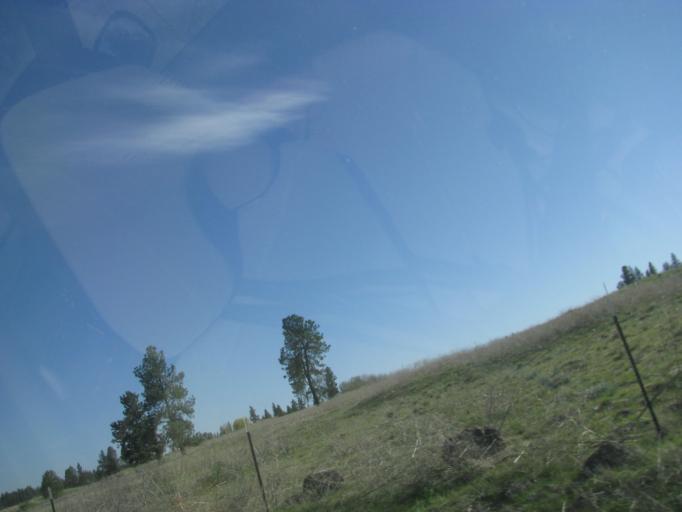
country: US
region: Washington
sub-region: Spokane County
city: Medical Lake
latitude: 47.3600
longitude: -117.8273
